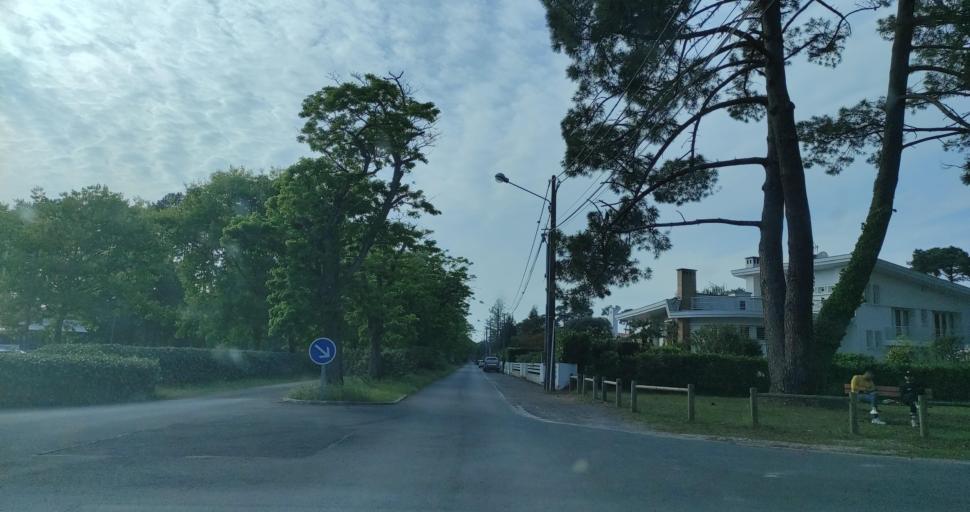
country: FR
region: Aquitaine
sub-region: Departement de la Gironde
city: Ares
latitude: 44.7537
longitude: -1.1279
